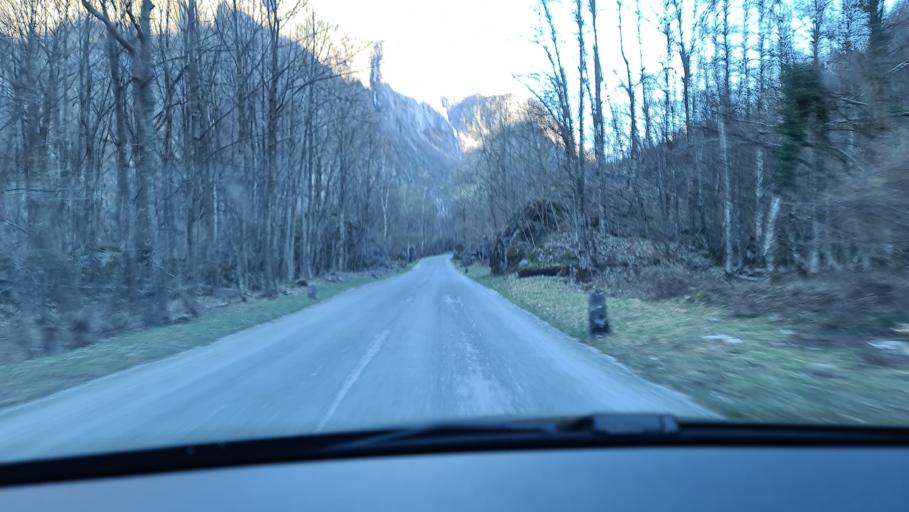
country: IT
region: Piedmont
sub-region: Provincia Verbano-Cusio-Ossola
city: Formazza
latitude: 46.4052
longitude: 8.5284
